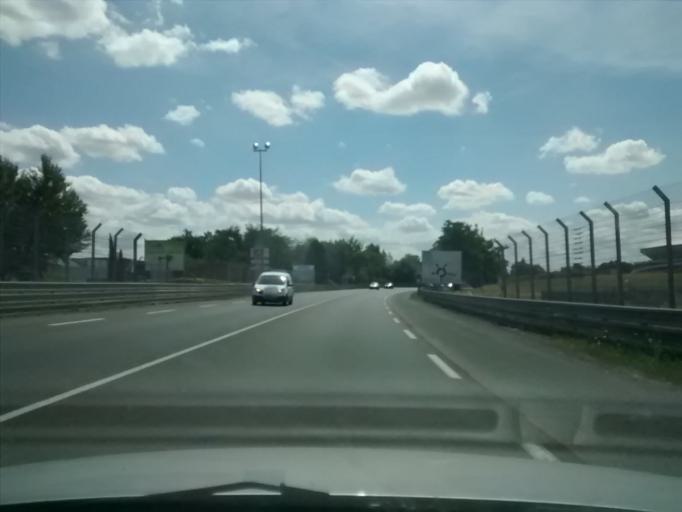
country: FR
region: Pays de la Loire
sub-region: Departement de la Sarthe
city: Ruaudin
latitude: 47.9580
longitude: 0.2267
